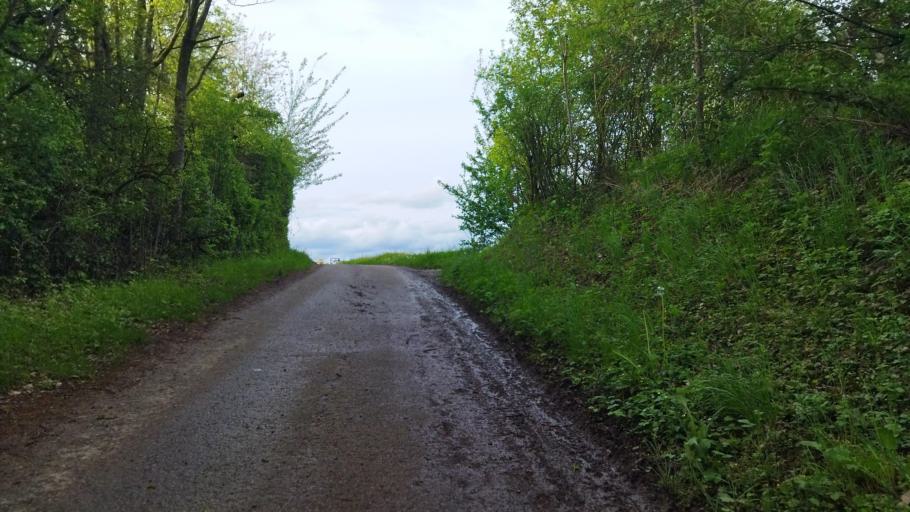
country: DE
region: Baden-Wuerttemberg
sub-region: Regierungsbezirk Stuttgart
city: Ilsfeld
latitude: 49.0728
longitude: 9.2500
